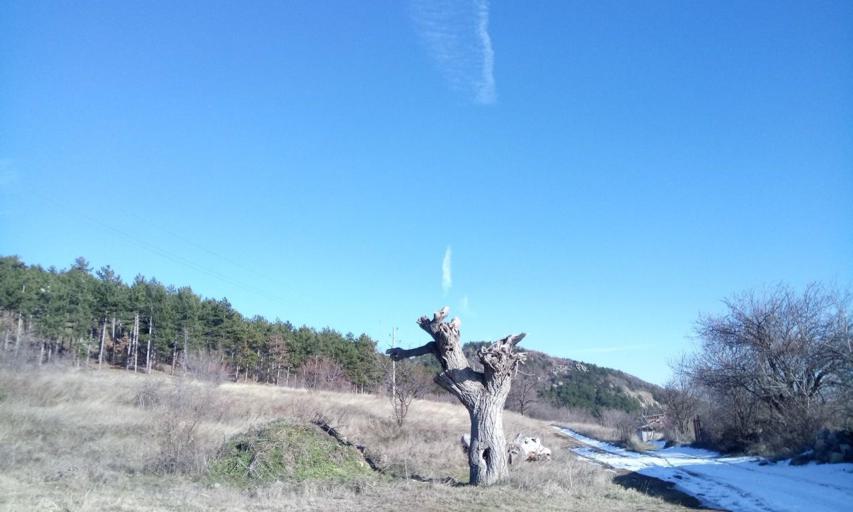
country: BG
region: Plovdiv
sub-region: Obshtina Khisarya
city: Khisarya
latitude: 42.5255
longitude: 24.7150
